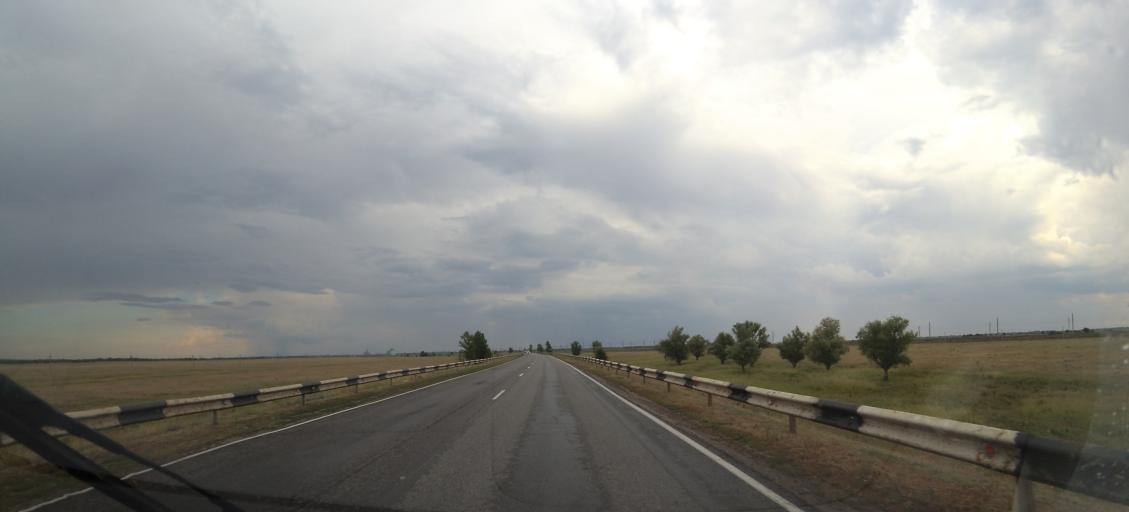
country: RU
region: Rostov
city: Dubovskoye
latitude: 47.3841
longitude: 42.6992
